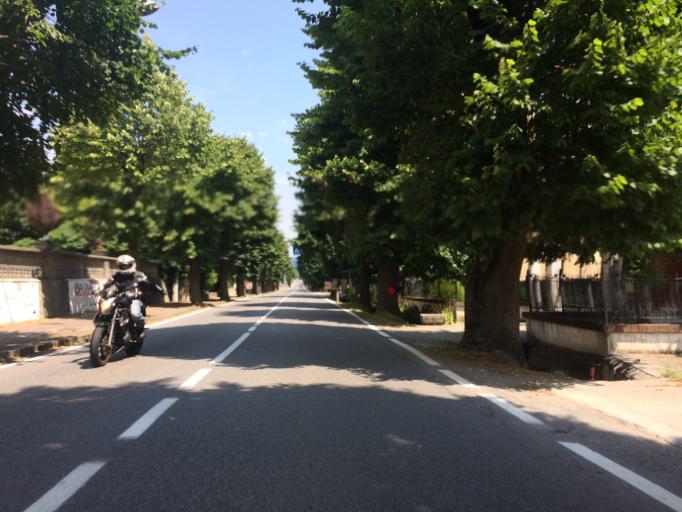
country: IT
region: Piedmont
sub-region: Provincia di Cuneo
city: Bagnasco
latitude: 44.3030
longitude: 8.0447
